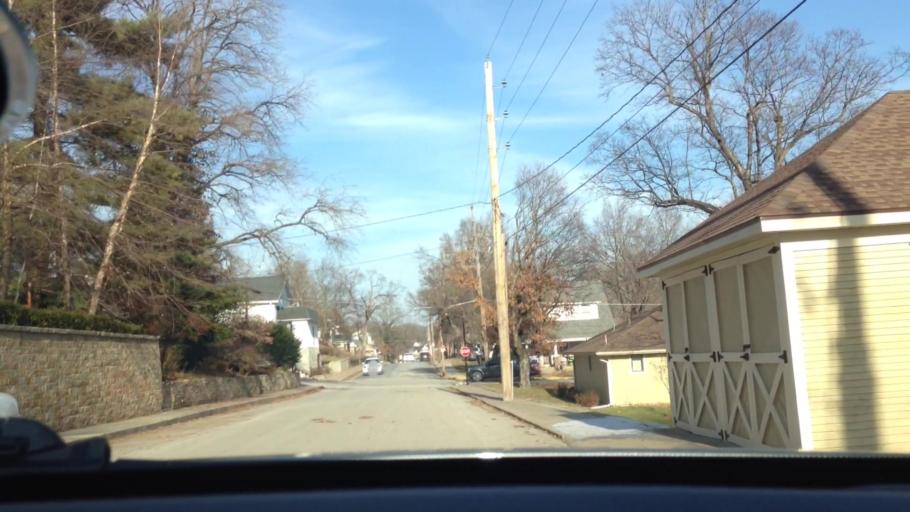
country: US
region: Missouri
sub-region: Platte County
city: Weston
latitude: 39.4117
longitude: -94.9044
